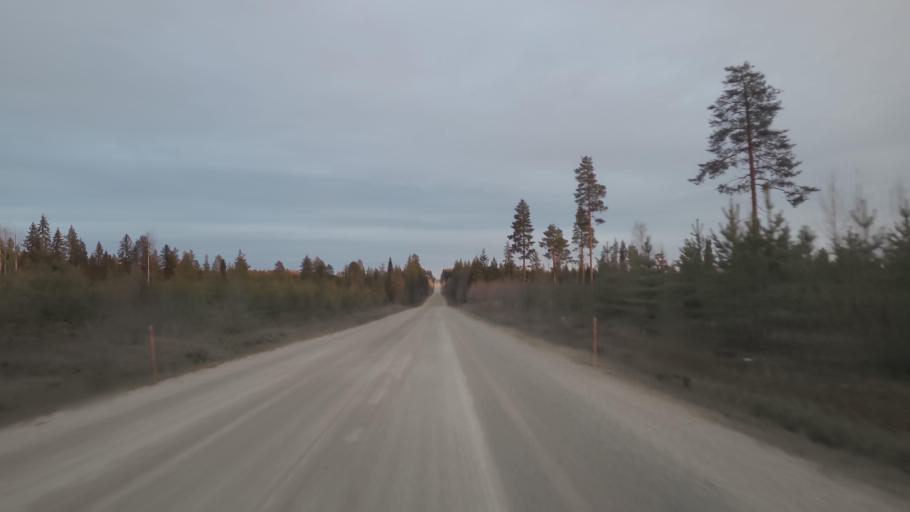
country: FI
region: Lapland
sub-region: Kemi-Tornio
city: Tervola
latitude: 66.0641
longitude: 24.9165
